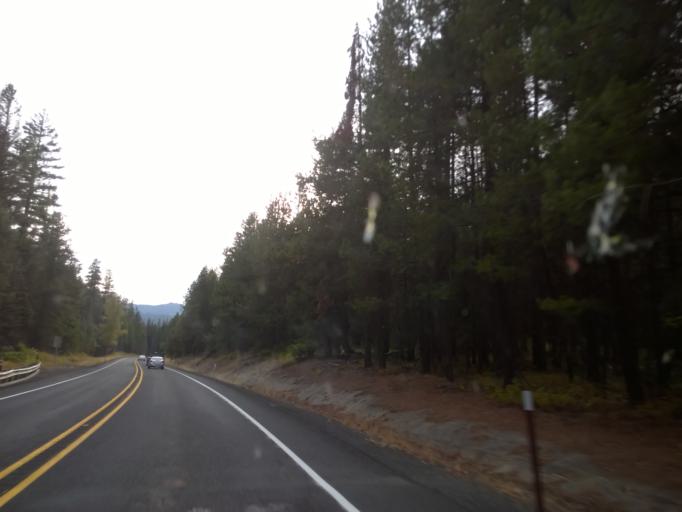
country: US
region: Washington
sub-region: Chelan County
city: Cashmere
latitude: 47.3348
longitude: -120.6301
